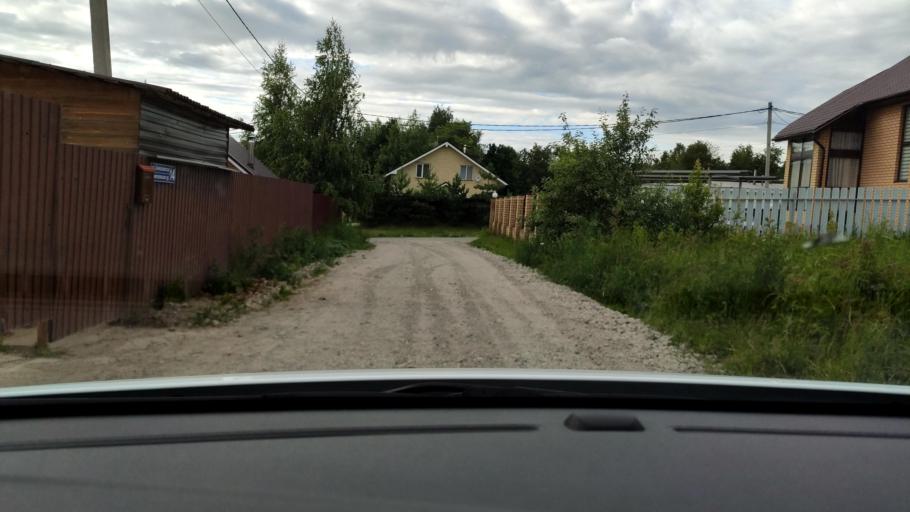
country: RU
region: Tatarstan
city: Stolbishchi
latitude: 55.7613
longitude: 49.3011
